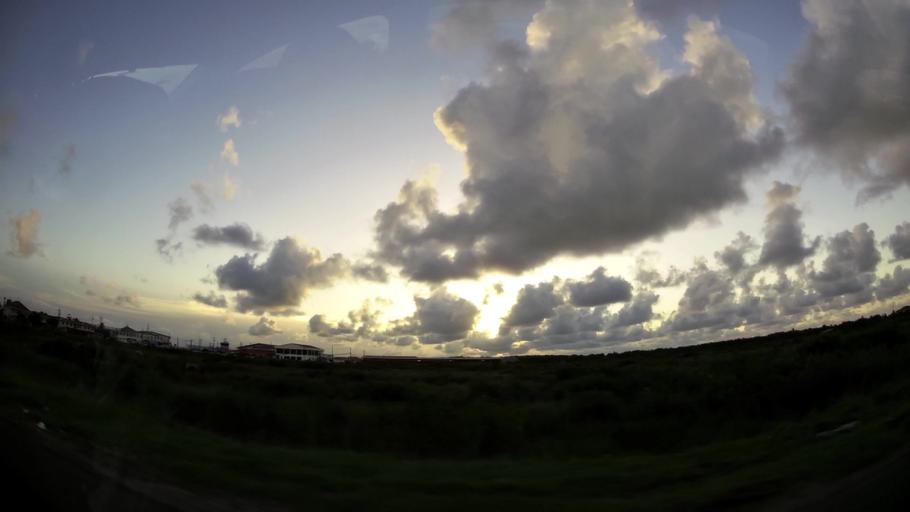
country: GY
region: Demerara-Mahaica
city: Georgetown
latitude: 6.8079
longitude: -58.1008
